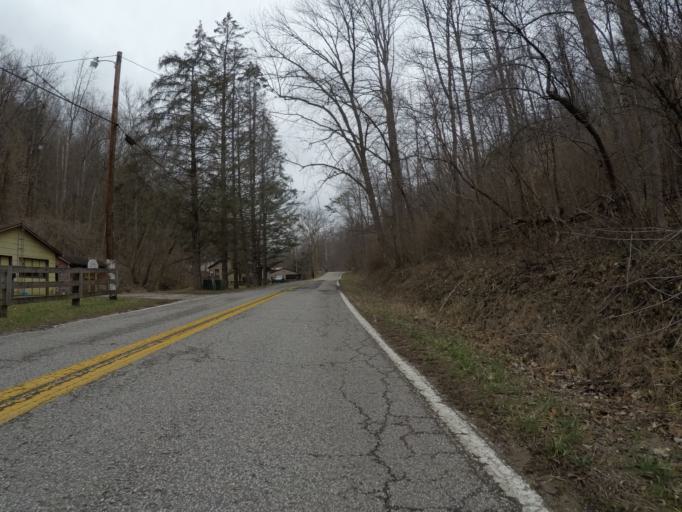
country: US
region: West Virginia
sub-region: Cabell County
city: Barboursville
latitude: 38.4480
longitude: -82.2568
